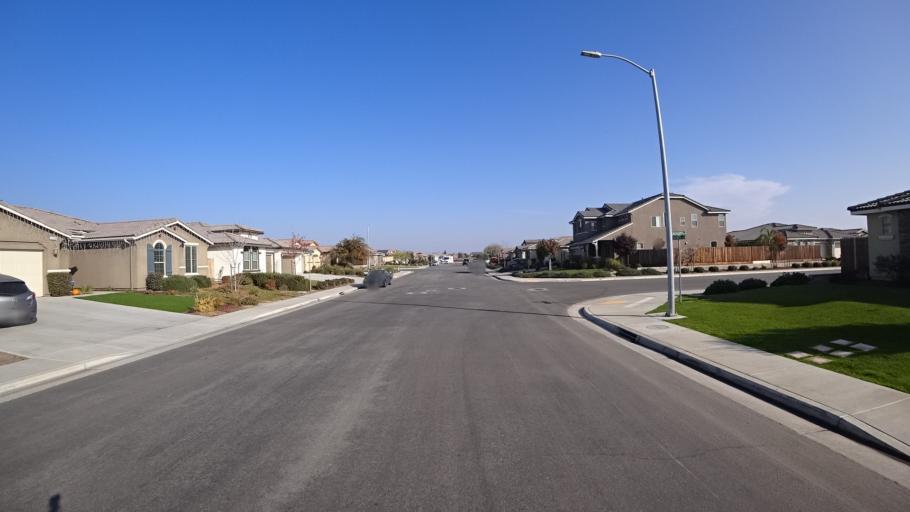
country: US
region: California
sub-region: Kern County
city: Rosedale
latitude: 35.3530
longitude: -119.1707
